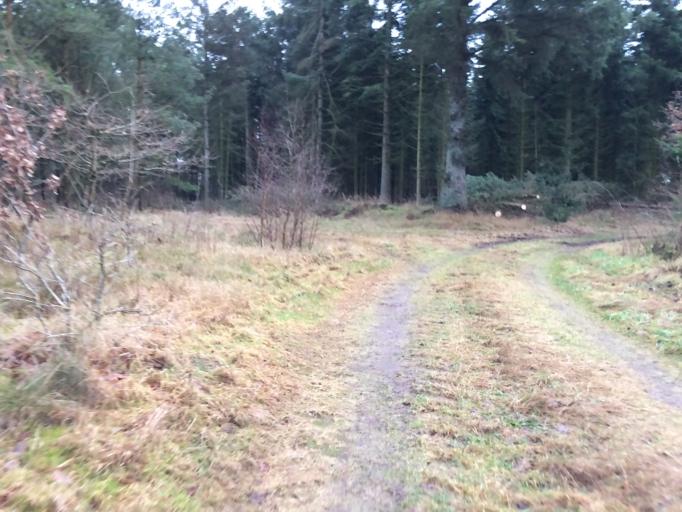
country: DK
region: Central Jutland
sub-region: Holstebro Kommune
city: Ulfborg
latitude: 56.2640
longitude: 8.2599
